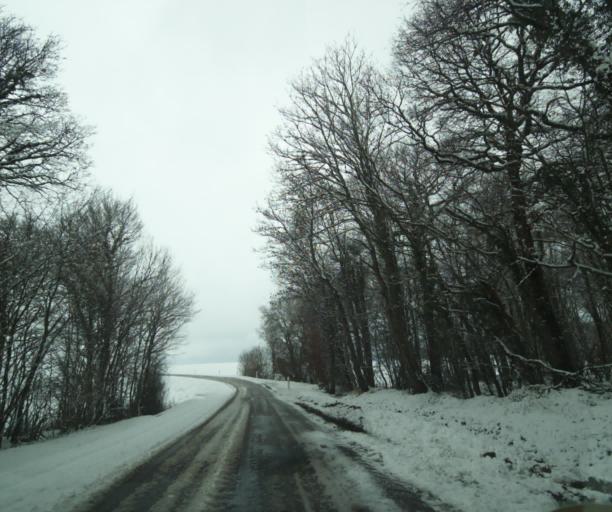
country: FR
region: Champagne-Ardenne
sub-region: Departement de la Haute-Marne
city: Laneuville-a-Remy
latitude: 48.3950
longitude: 4.8669
